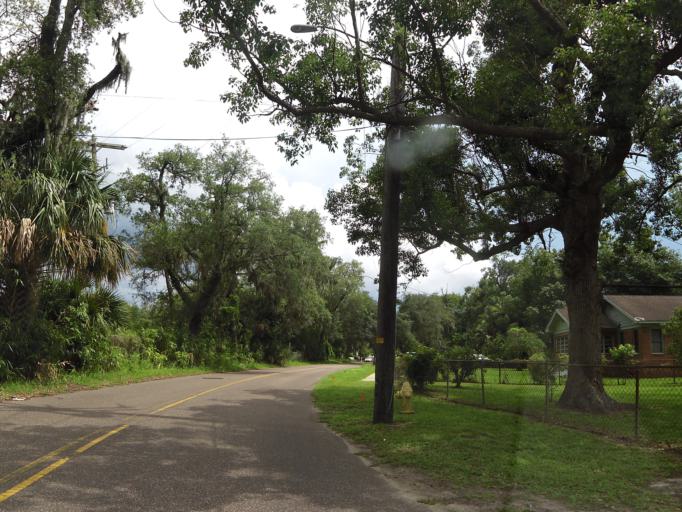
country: US
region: Florida
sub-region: Duval County
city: Jacksonville
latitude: 30.3876
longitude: -81.6406
